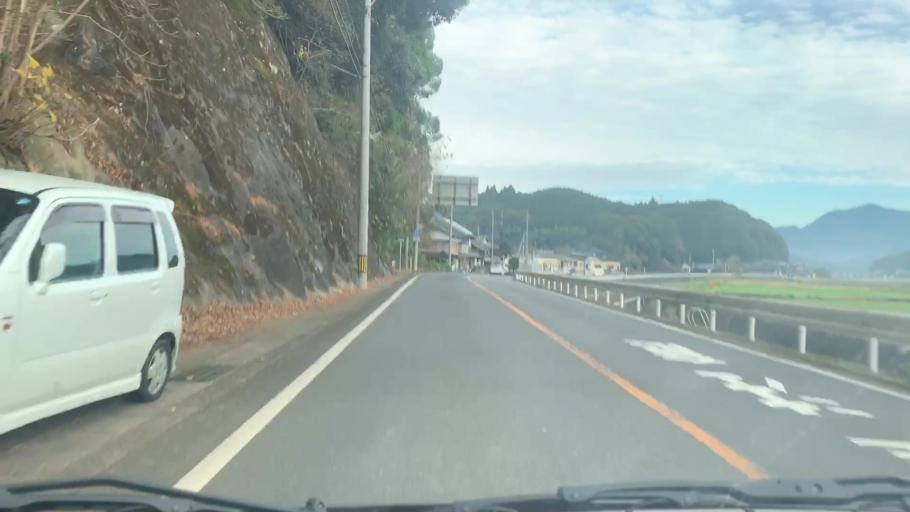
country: JP
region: Saga Prefecture
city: Takeocho-takeo
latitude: 33.2276
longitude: 129.9638
